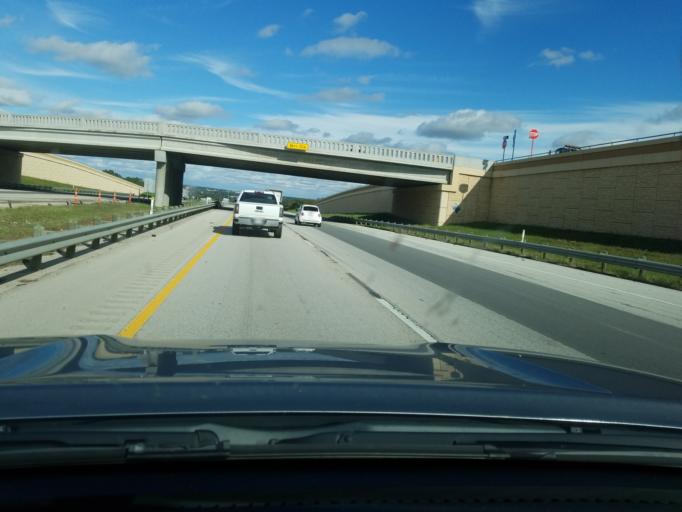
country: US
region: Texas
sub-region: Parker County
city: Weatherford
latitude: 32.7327
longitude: -97.7749
